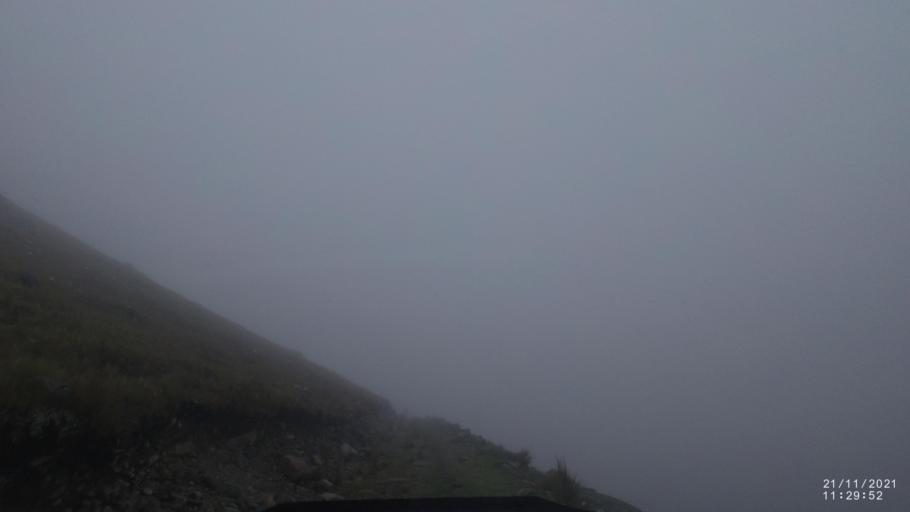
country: BO
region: Cochabamba
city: Cochabamba
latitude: -16.9622
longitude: -66.2674
